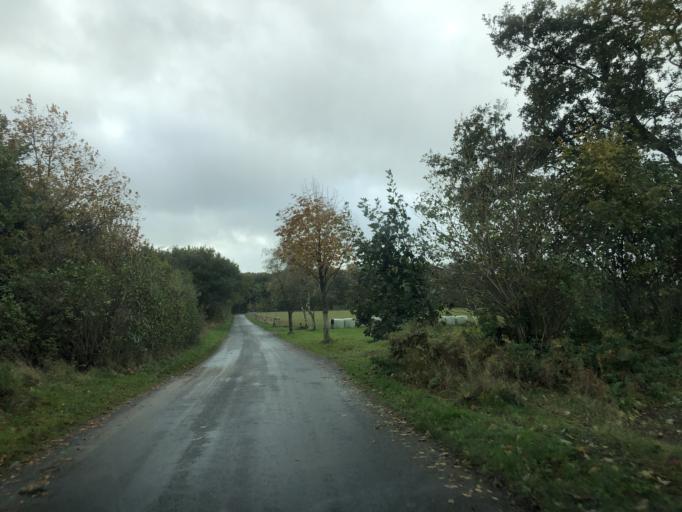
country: DK
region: South Denmark
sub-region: Vejen Kommune
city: Vejen
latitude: 55.4506
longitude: 9.1101
